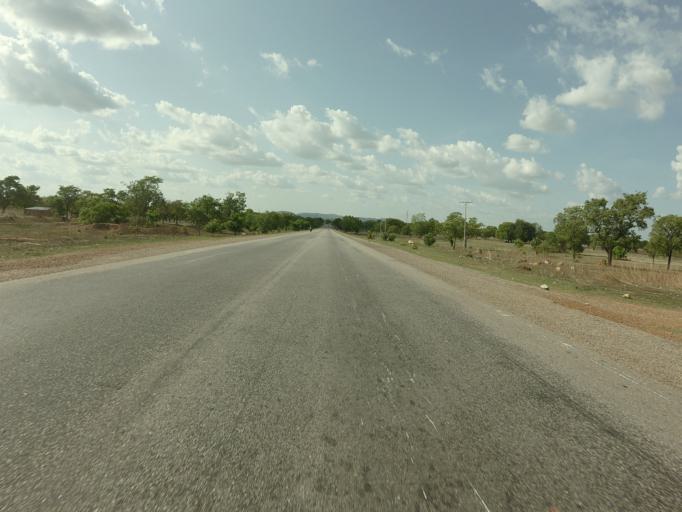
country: GH
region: Upper East
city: Bolgatanga
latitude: 10.5736
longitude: -0.8328
